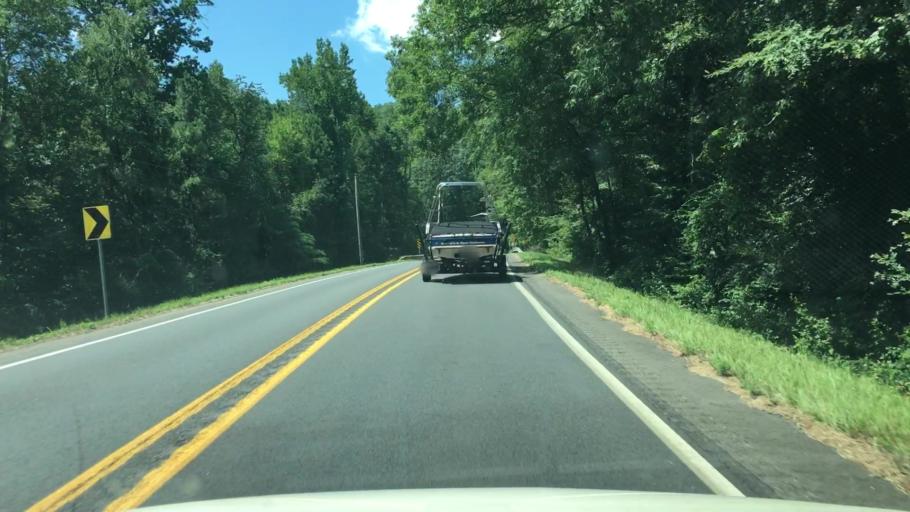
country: US
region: Arkansas
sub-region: Garland County
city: Lake Hamilton
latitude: 34.3404
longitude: -93.1831
